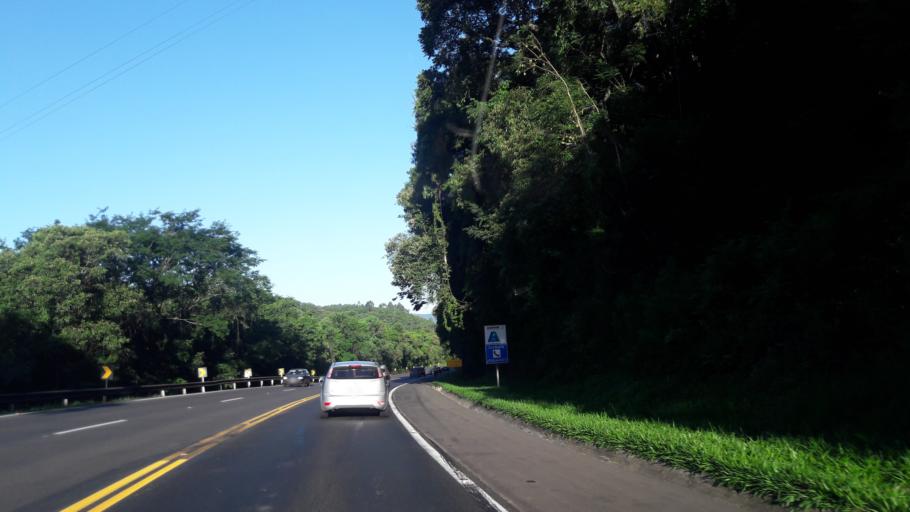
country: BR
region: Parana
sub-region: Prudentopolis
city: Prudentopolis
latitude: -25.3126
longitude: -51.1864
